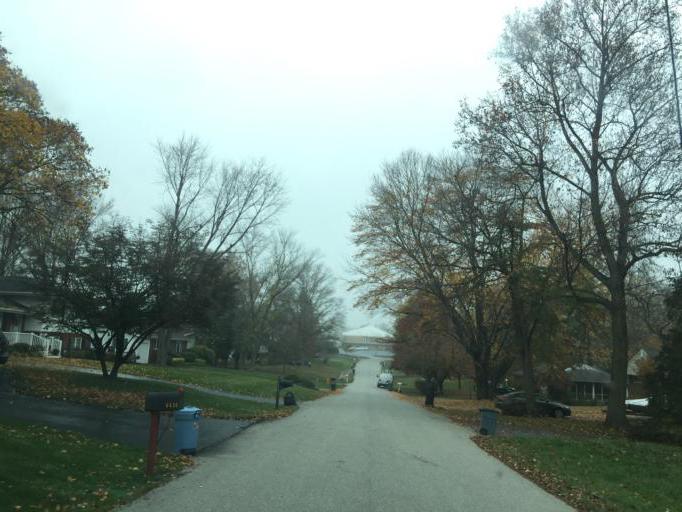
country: US
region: Maryland
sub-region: Howard County
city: Riverside
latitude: 39.1914
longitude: -76.8632
